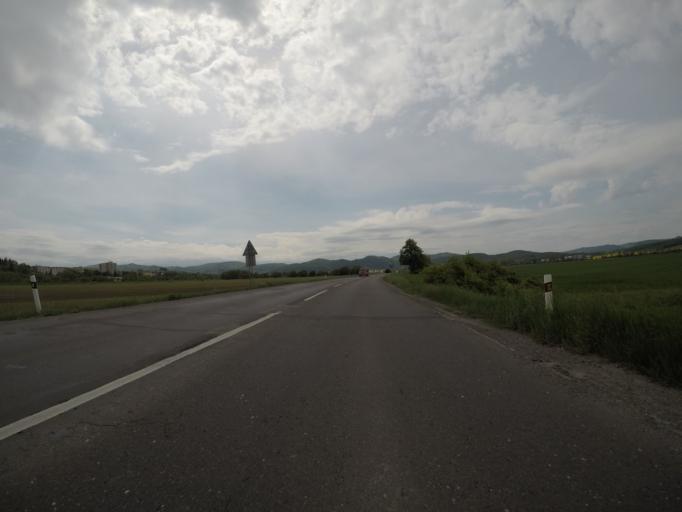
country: SK
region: Banskobystricky
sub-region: Okres Banska Bystrica
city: Zvolen
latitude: 48.5997
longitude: 19.1248
